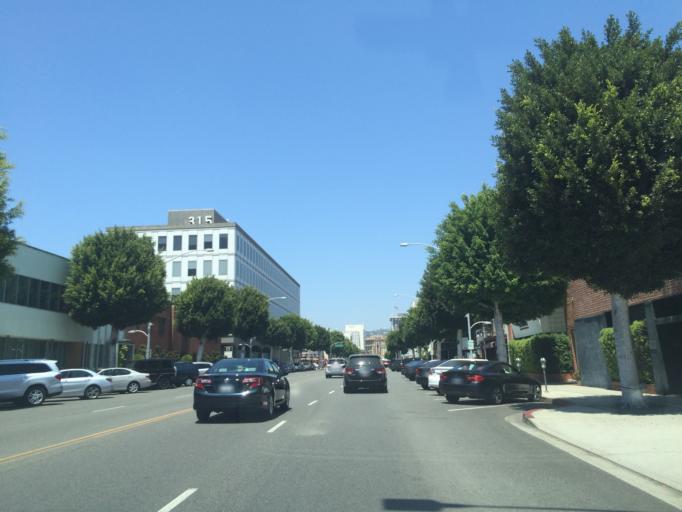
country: US
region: California
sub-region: Los Angeles County
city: Beverly Hills
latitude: 34.0606
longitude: -118.3990
